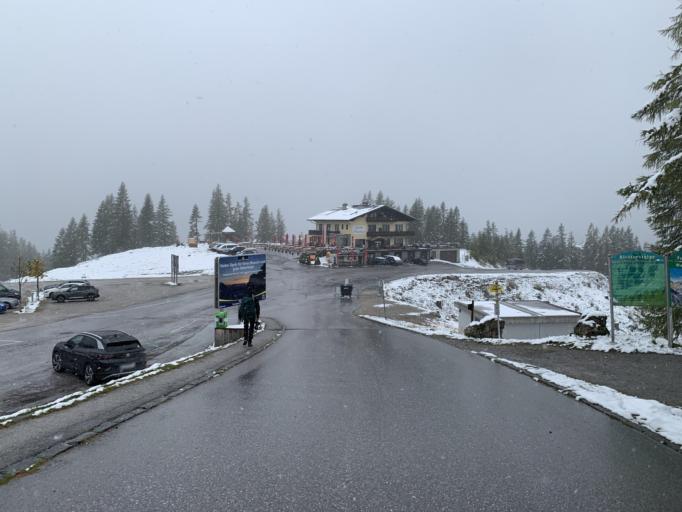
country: AT
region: Styria
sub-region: Politischer Bezirk Liezen
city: Schladming
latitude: 47.4507
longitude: 13.6173
